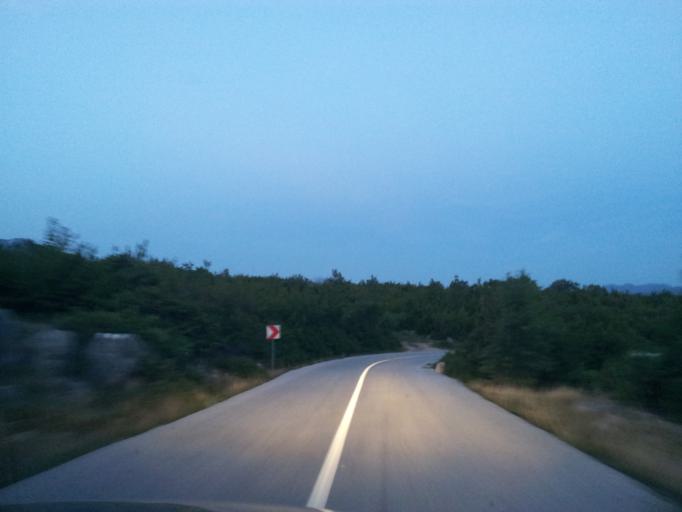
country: HR
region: Zadarska
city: Obrovac
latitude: 44.2240
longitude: 15.6709
